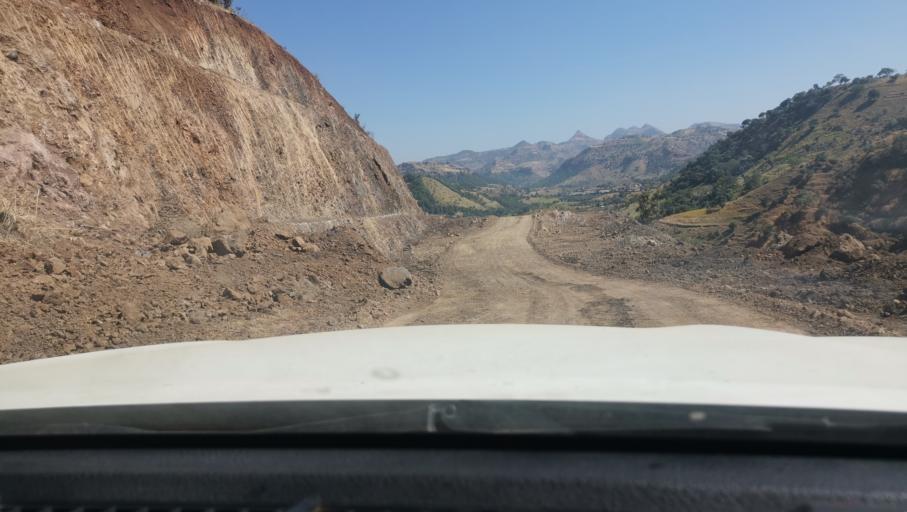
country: ET
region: Amhara
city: Debark'
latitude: 13.3044
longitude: 37.8309
